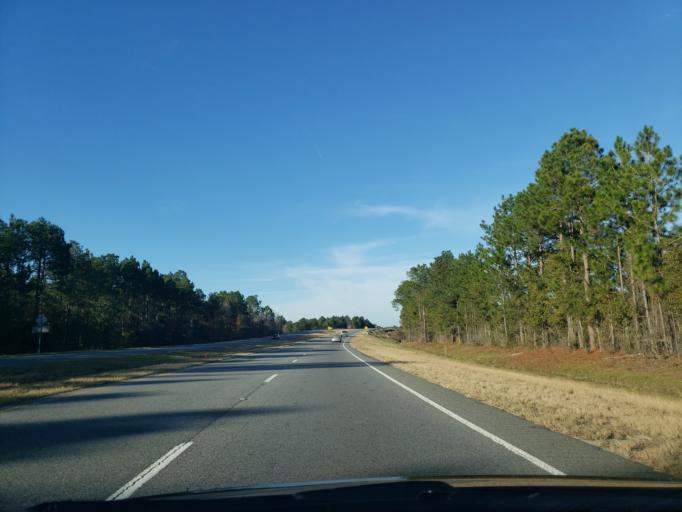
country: US
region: Georgia
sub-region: Ware County
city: Deenwood
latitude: 31.2294
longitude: -82.4266
